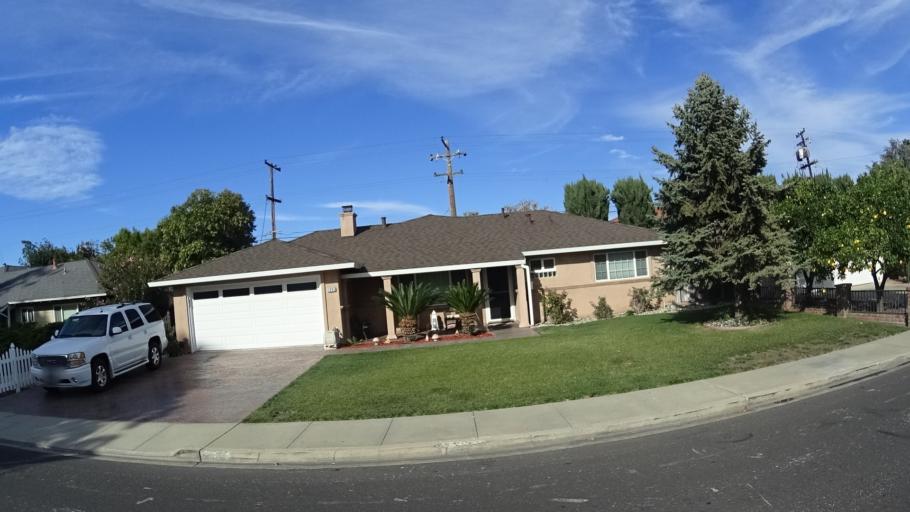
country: US
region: California
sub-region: Santa Clara County
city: Santa Clara
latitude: 37.3558
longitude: -121.9609
